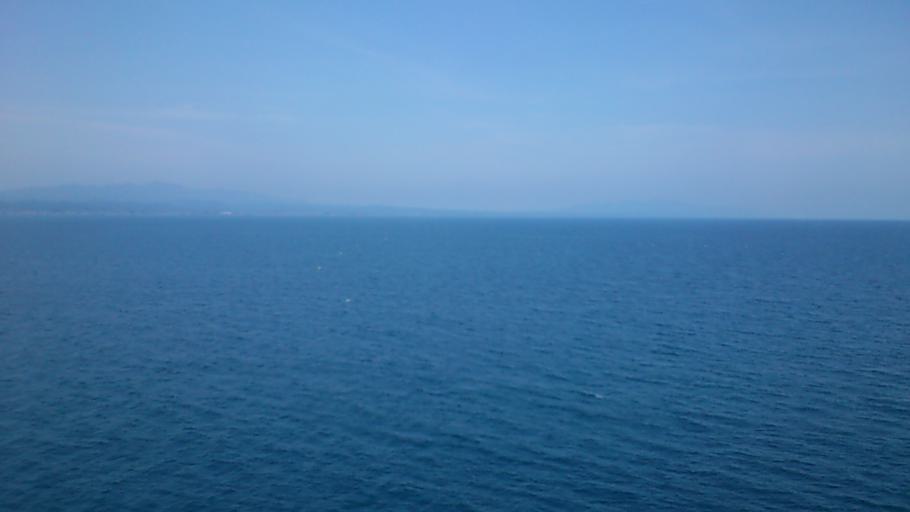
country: JP
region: Aomori
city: Aomori Shi
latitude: 40.8603
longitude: 140.7332
